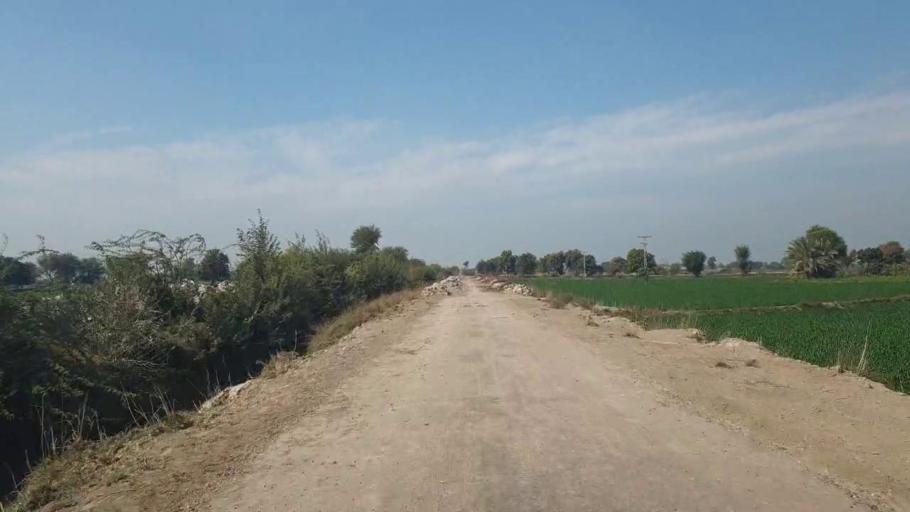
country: PK
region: Sindh
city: Shahdadpur
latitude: 25.9990
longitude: 68.5205
